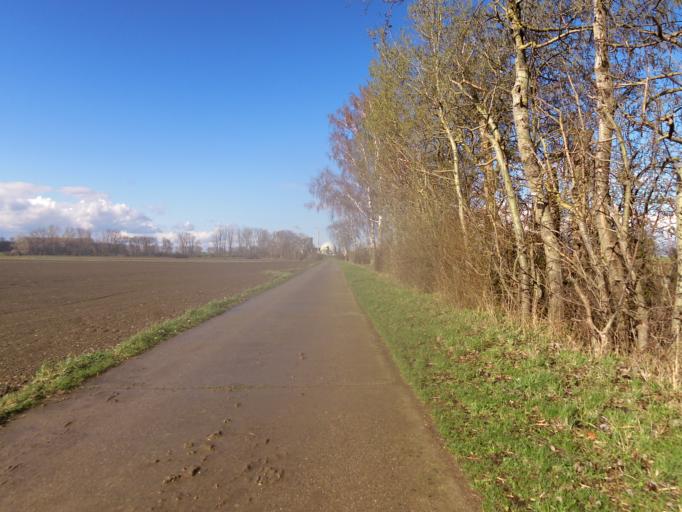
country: DE
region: Hesse
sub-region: Regierungsbezirk Darmstadt
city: Biblis
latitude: 49.6929
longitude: 8.4102
